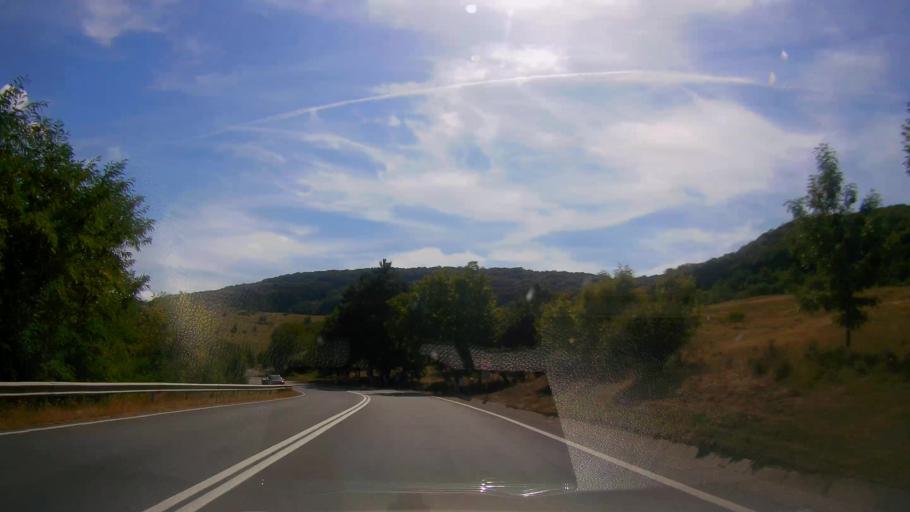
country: RO
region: Mures
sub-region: Comuna Nades
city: Nades
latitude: 46.2905
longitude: 24.7161
